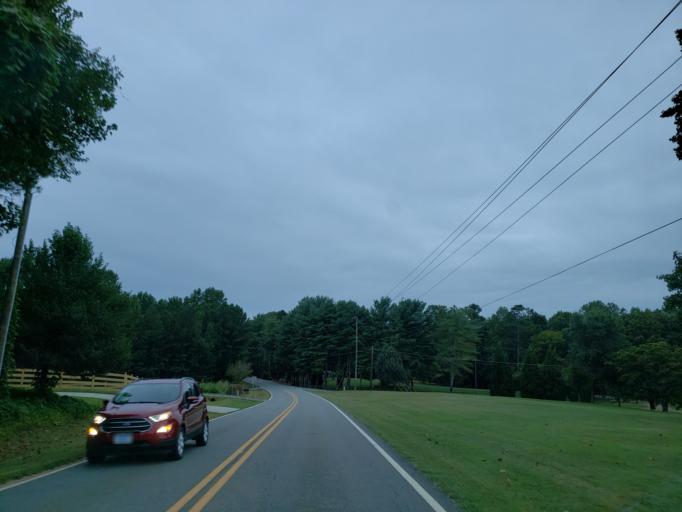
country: US
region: Georgia
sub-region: Cherokee County
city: Canton
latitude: 34.3456
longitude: -84.4917
